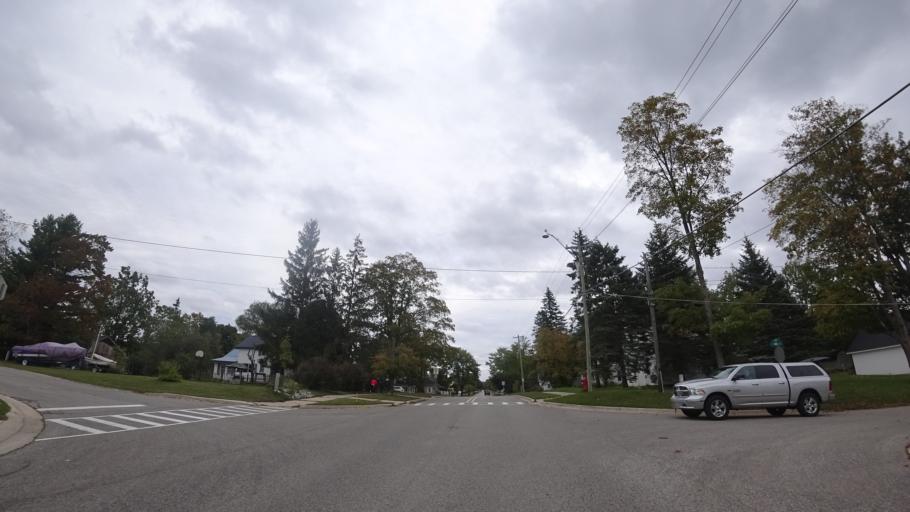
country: US
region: Michigan
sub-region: Emmet County
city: Harbor Springs
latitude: 45.4353
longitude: -84.9961
